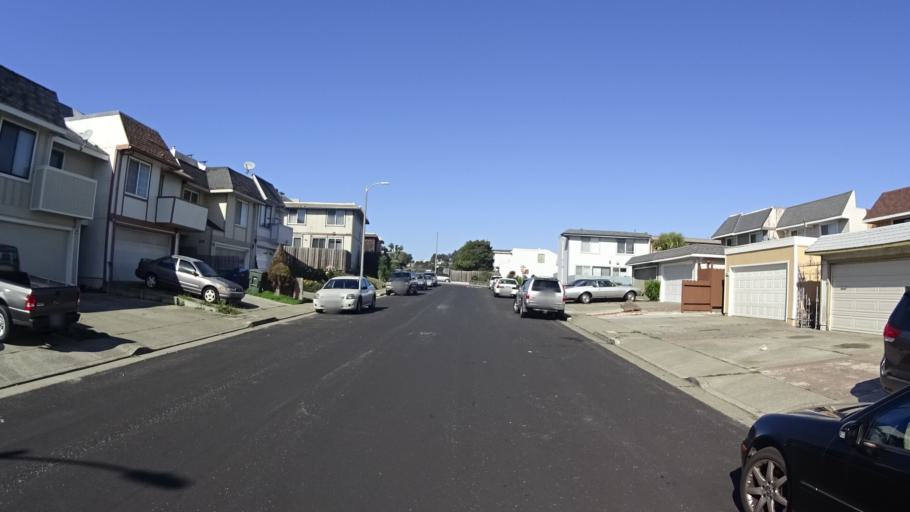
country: US
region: California
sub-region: San Mateo County
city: Colma
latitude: 37.6456
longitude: -122.4615
